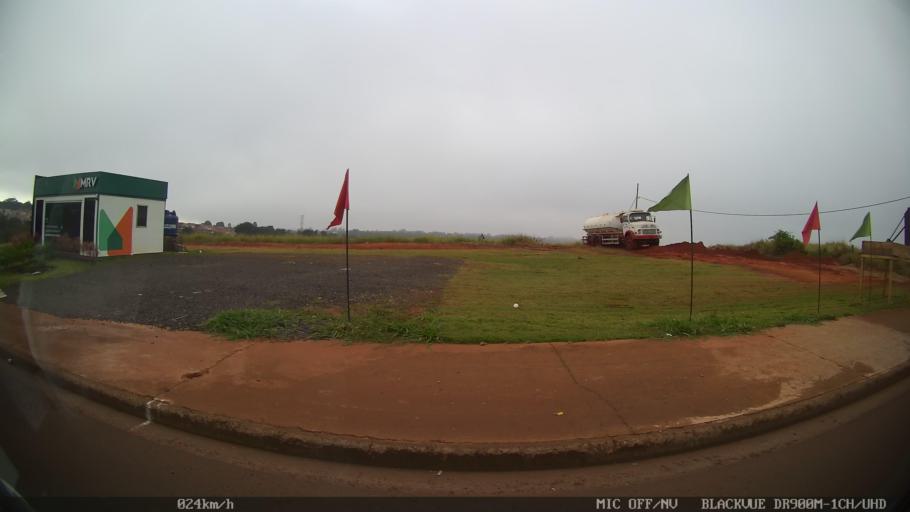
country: BR
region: Sao Paulo
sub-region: Sao Jose Do Rio Preto
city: Sao Jose do Rio Preto
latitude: -20.8515
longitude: -49.3701
